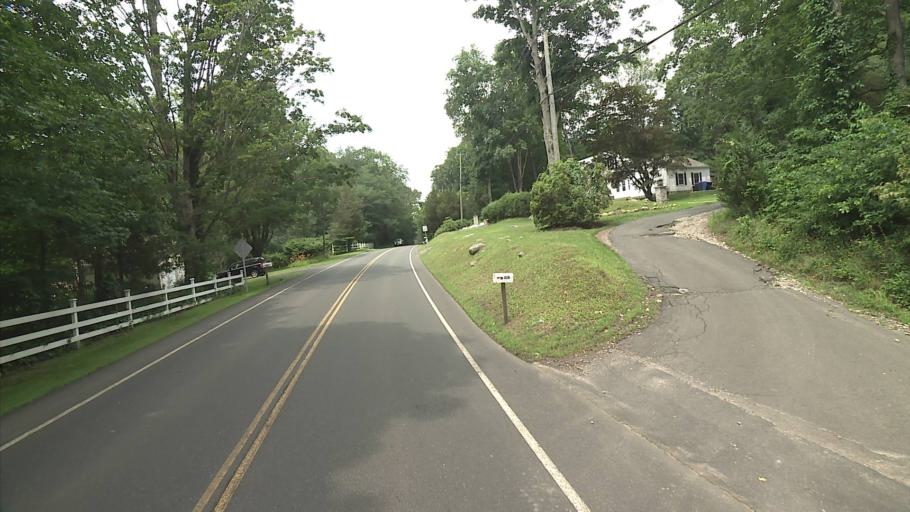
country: US
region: Connecticut
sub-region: New Haven County
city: Madison
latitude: 41.3155
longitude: -72.6025
